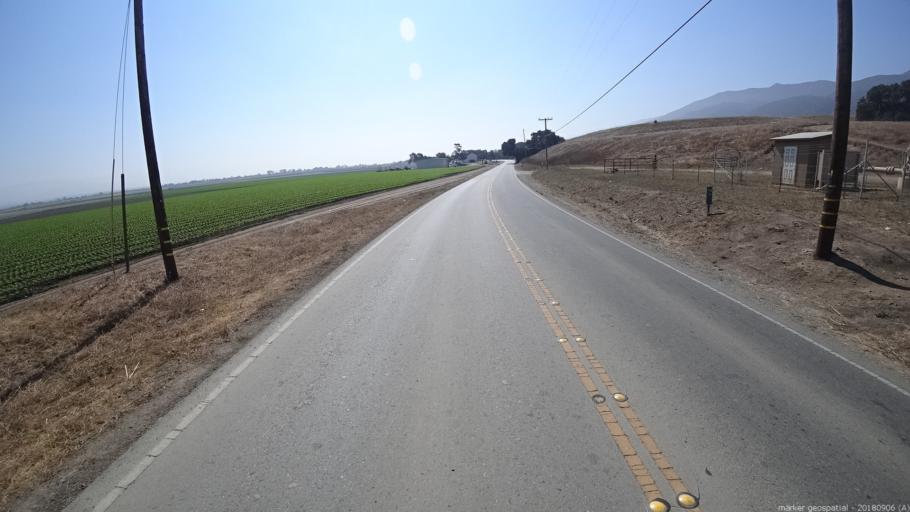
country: US
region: California
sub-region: Monterey County
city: Chualar
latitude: 36.5703
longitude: -121.5708
